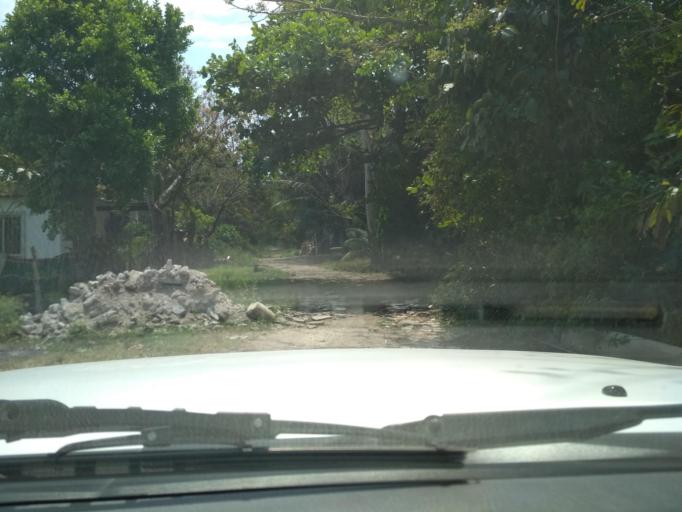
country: MX
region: Veracruz
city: Anton Lizardo
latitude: 19.0064
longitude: -95.9882
